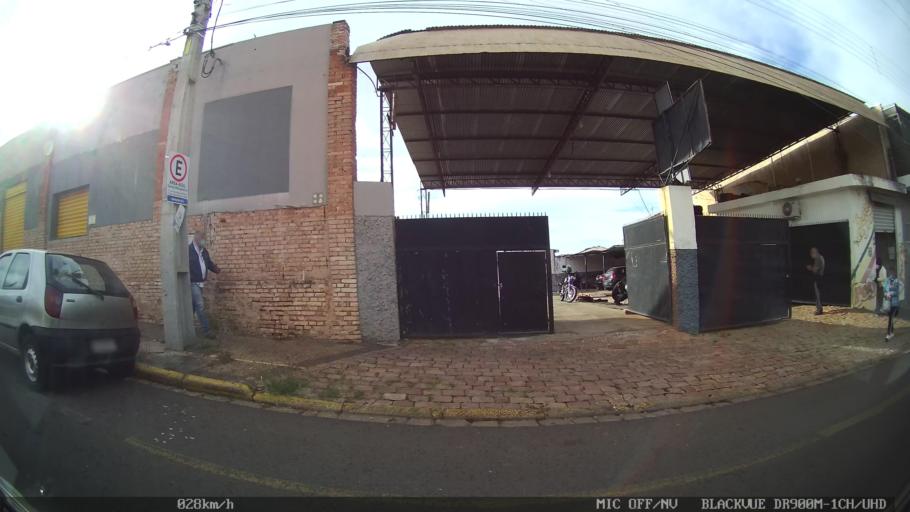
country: BR
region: Sao Paulo
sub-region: Catanduva
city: Catanduva
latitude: -21.1439
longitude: -48.9753
